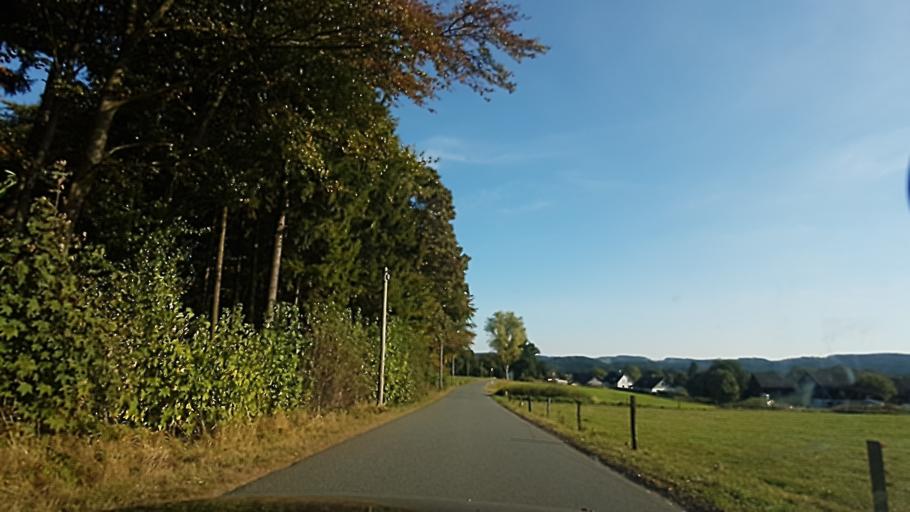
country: DE
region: North Rhine-Westphalia
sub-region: Regierungsbezirk Koln
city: Marienheide
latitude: 51.1242
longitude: 7.4859
